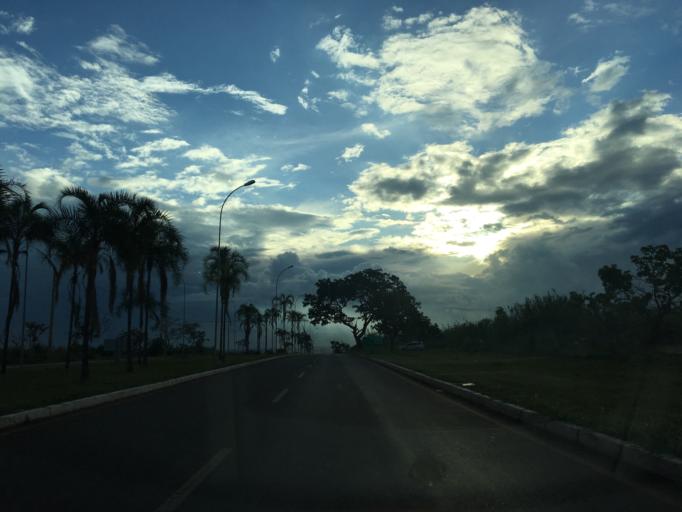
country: BR
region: Federal District
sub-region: Brasilia
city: Brasilia
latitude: -15.8086
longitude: -47.8411
